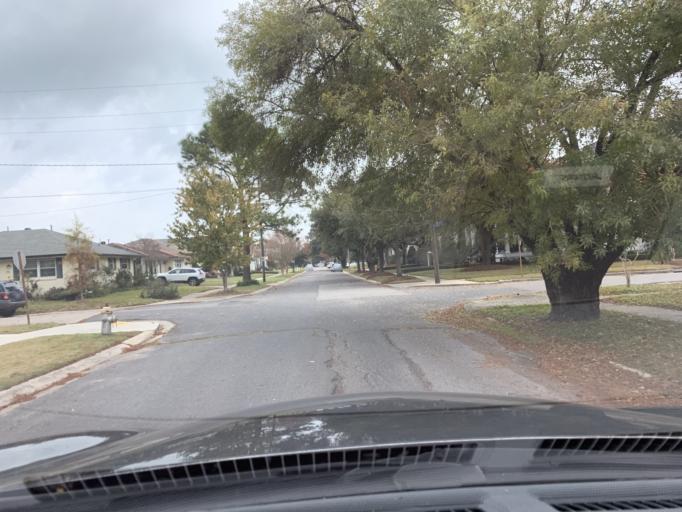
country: US
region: Louisiana
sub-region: Jefferson Parish
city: Metairie
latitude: 30.0060
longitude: -90.1013
